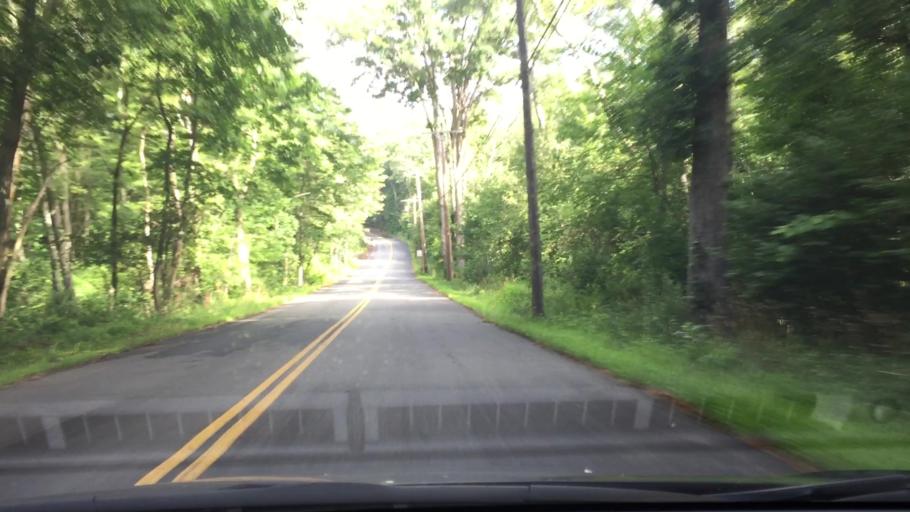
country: US
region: Massachusetts
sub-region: Middlesex County
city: Acton
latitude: 42.4918
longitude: -71.4343
